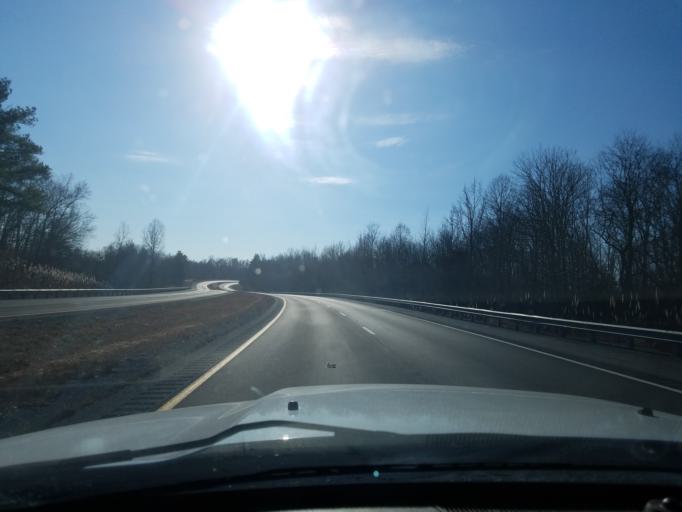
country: US
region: Kentucky
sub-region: Muhlenberg County
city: Central City
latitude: 37.3083
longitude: -87.0610
